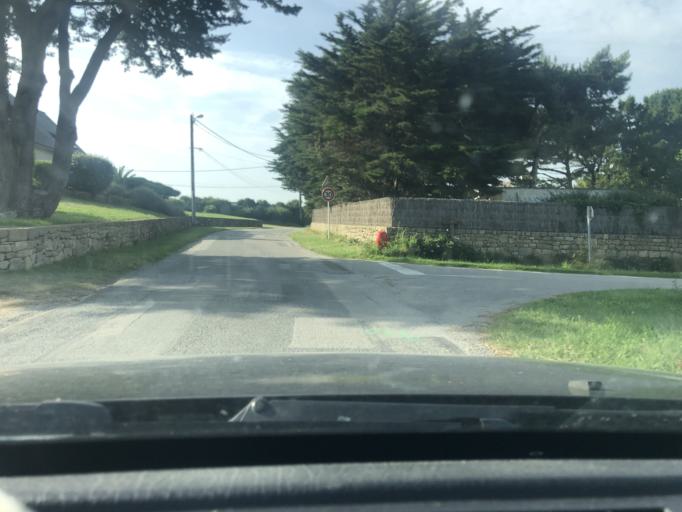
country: FR
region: Brittany
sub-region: Departement du Morbihan
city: Erdeven
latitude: 47.6249
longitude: -3.1802
